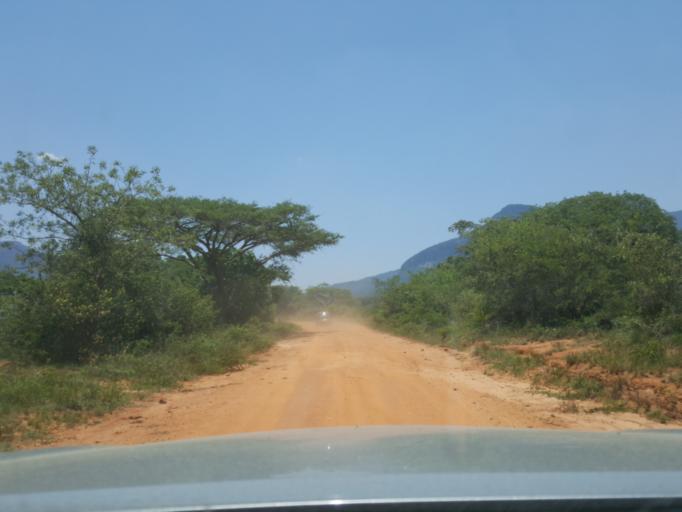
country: ZA
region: Limpopo
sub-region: Mopani District Municipality
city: Hoedspruit
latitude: -24.5881
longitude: 30.9540
